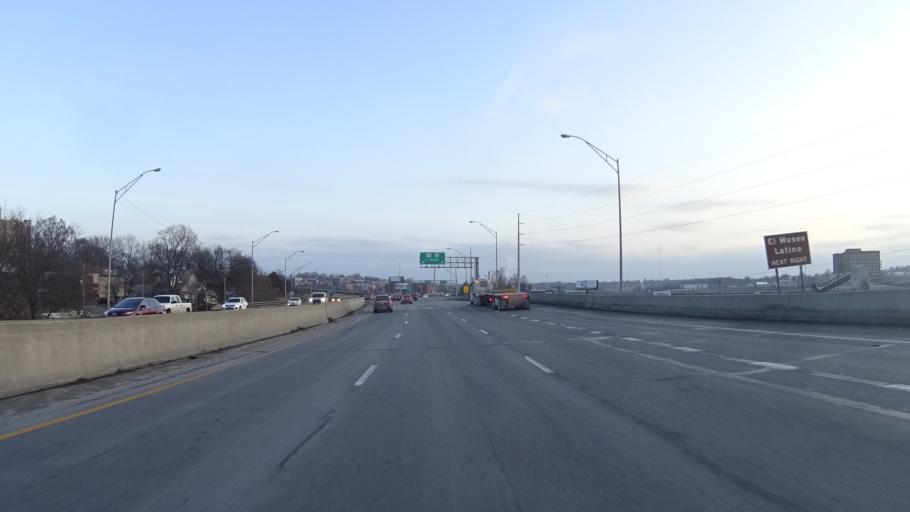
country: US
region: Nebraska
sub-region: Douglas County
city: Omaha
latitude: 41.2155
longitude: -95.9531
